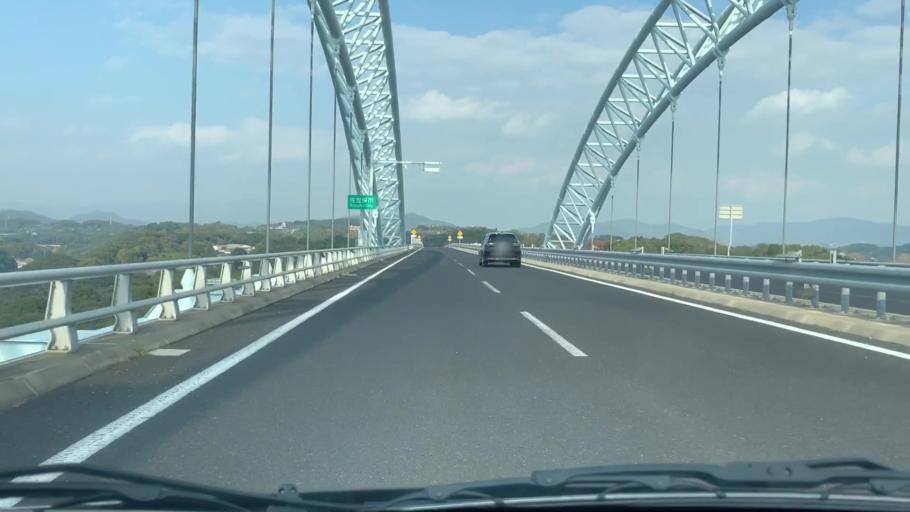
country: JP
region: Nagasaki
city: Sasebo
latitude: 33.0539
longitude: 129.7548
